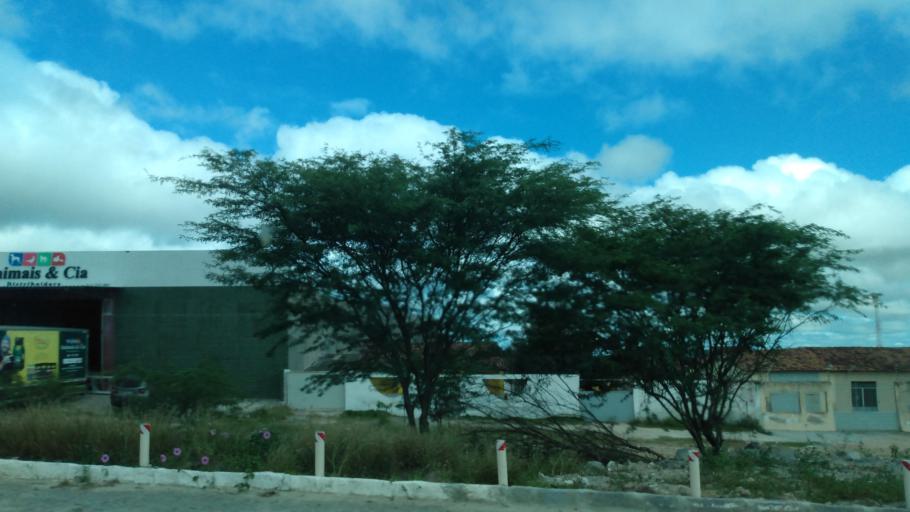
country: BR
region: Pernambuco
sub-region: Caruaru
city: Caruaru
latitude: -8.3092
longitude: -35.9902
